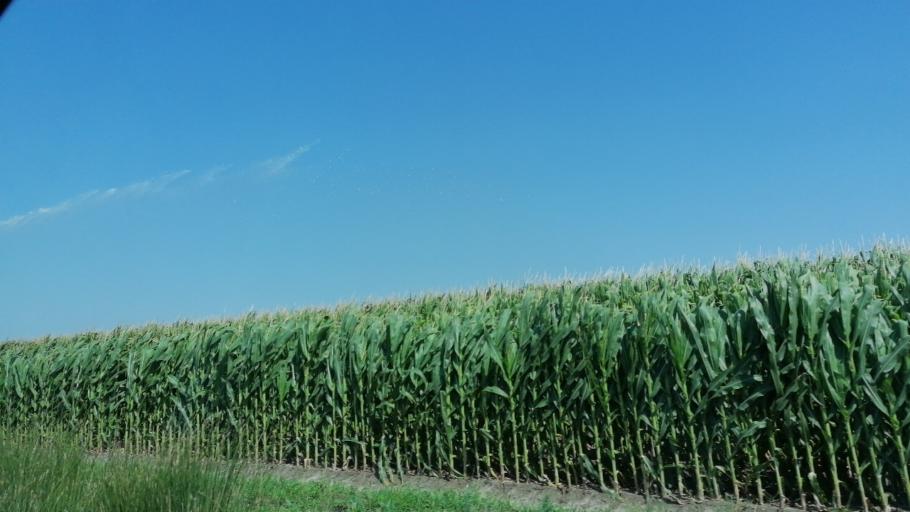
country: PT
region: Santarem
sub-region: Benavente
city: Poceirao
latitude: 38.6964
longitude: -8.7264
